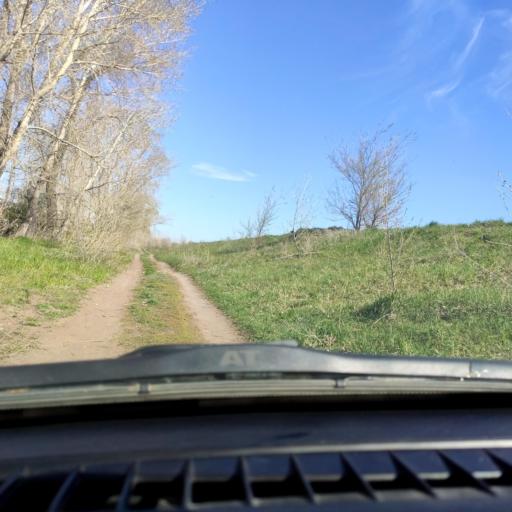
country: RU
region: Samara
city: Zhigulevsk
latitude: 53.4616
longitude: 49.5415
